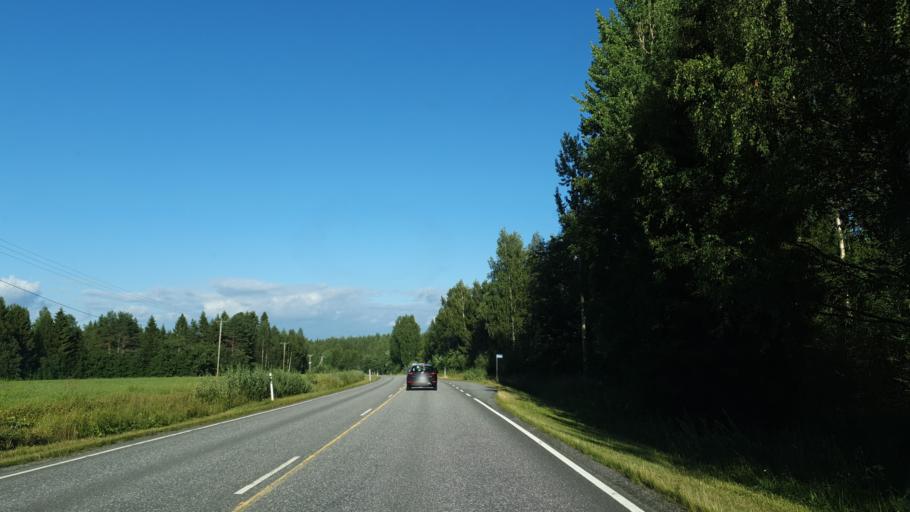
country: FI
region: North Karelia
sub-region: Joensuu
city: Outokumpu
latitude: 62.5336
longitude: 28.9294
